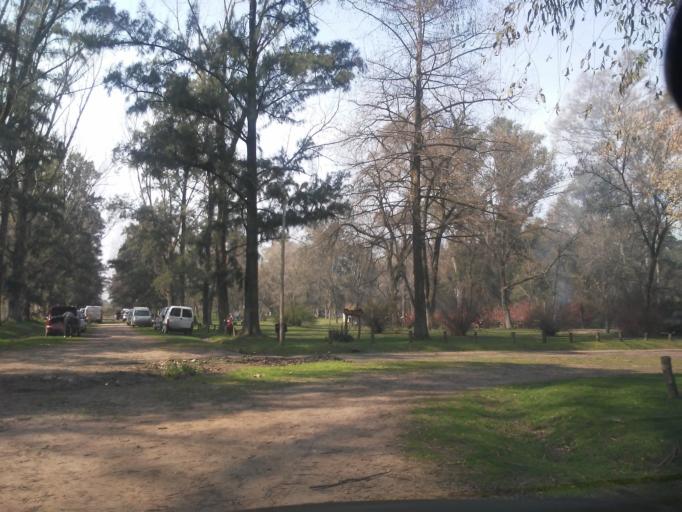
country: AR
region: Buenos Aires
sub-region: Partido de General Rodriguez
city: General Rodriguez
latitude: -34.6647
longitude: -58.8580
